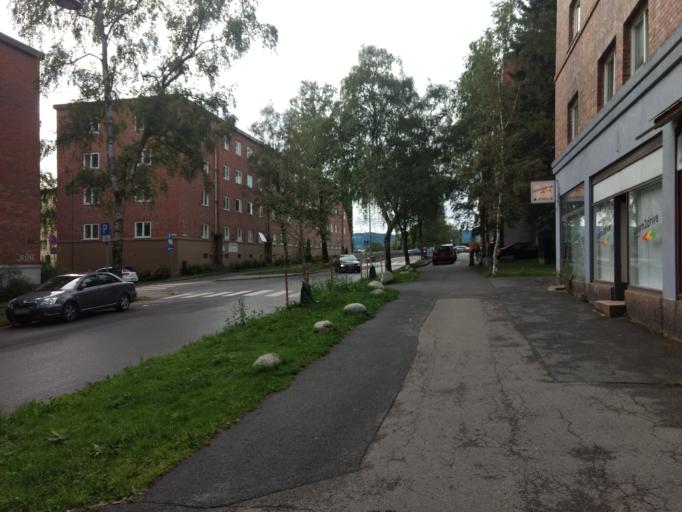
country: NO
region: Oslo
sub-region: Oslo
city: Oslo
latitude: 59.9339
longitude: 10.7814
